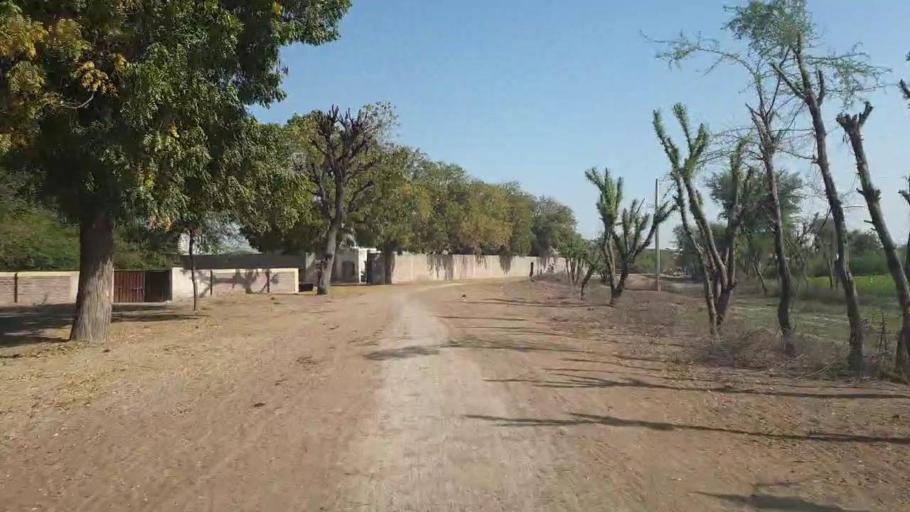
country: PK
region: Sindh
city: Umarkot
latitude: 25.3069
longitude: 69.6586
